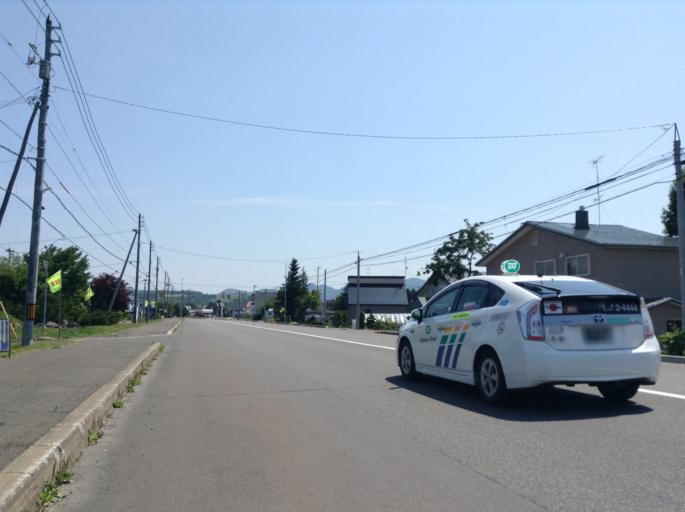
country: JP
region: Hokkaido
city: Nayoro
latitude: 44.3050
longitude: 142.6265
